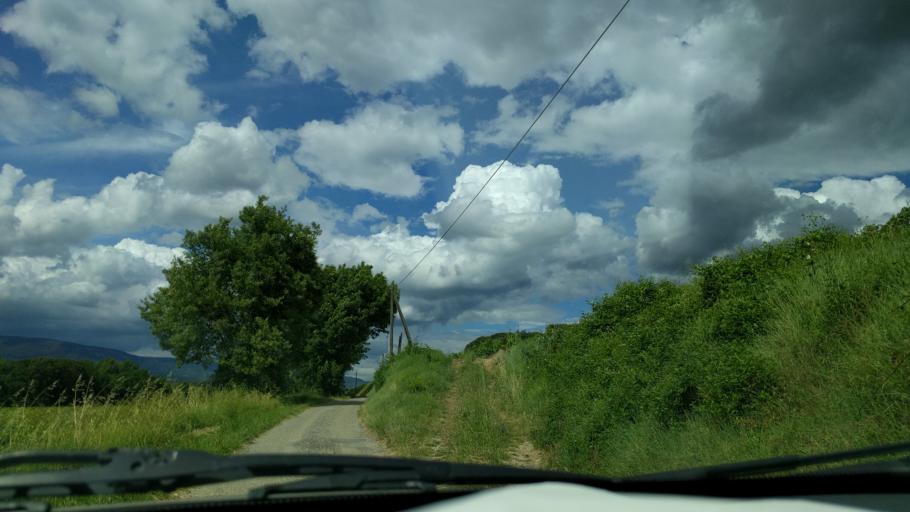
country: FR
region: Provence-Alpes-Cote d'Azur
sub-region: Departement du Vaucluse
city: Grambois
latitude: 43.7277
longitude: 5.5575
